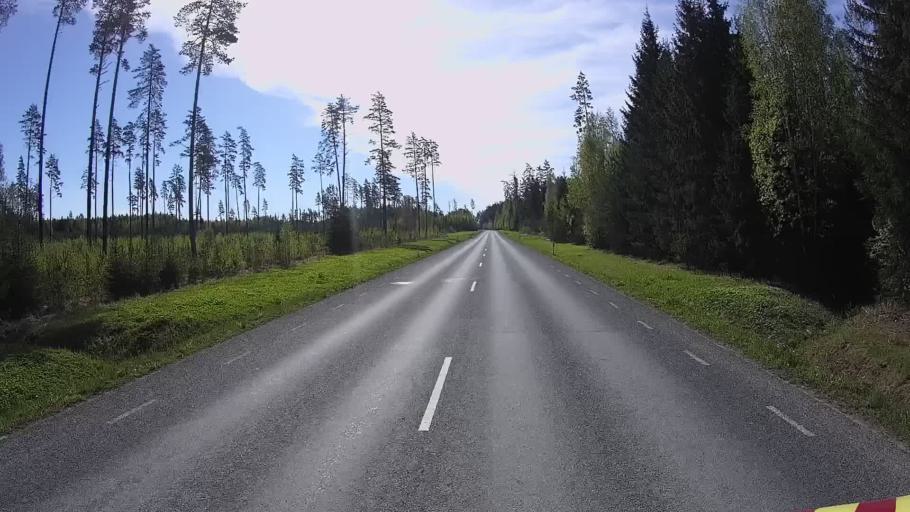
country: EE
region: Polvamaa
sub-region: Polva linn
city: Polva
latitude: 58.1674
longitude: 27.1446
